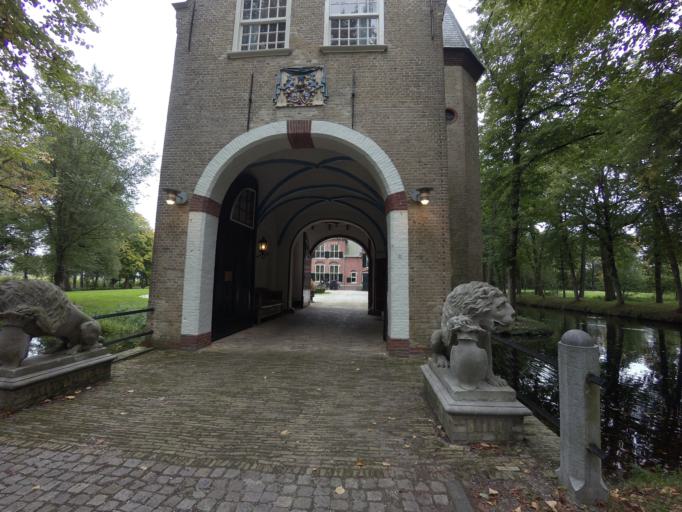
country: NL
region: Friesland
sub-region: Sudwest Fryslan
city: Sneek
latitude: 53.0407
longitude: 5.6329
